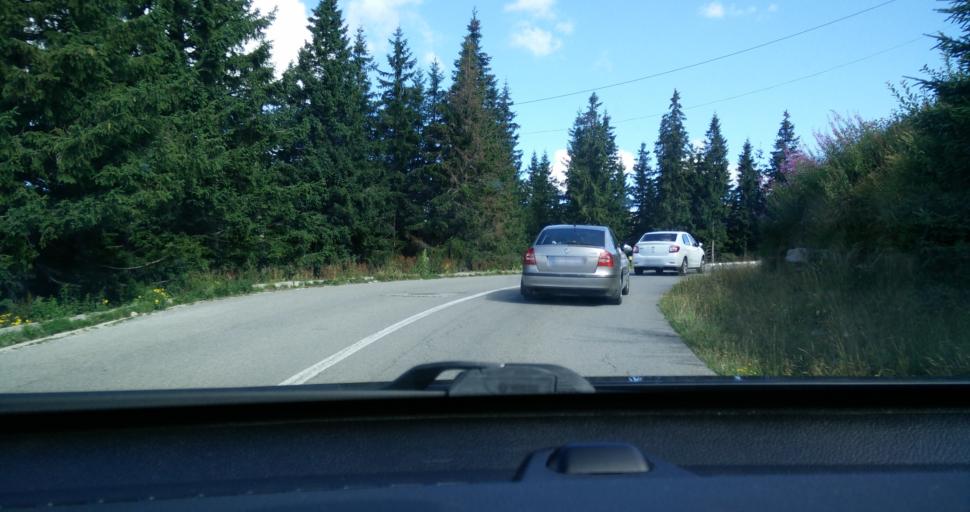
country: RO
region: Gorj
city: Novaci-Straini
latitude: 45.2987
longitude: 23.6805
